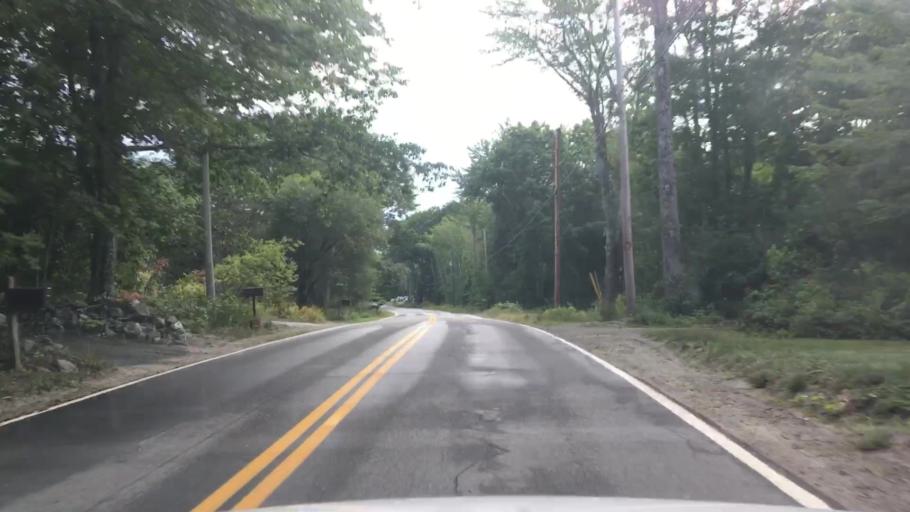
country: US
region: Maine
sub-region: Hancock County
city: Trenton
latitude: 44.4663
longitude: -68.4235
